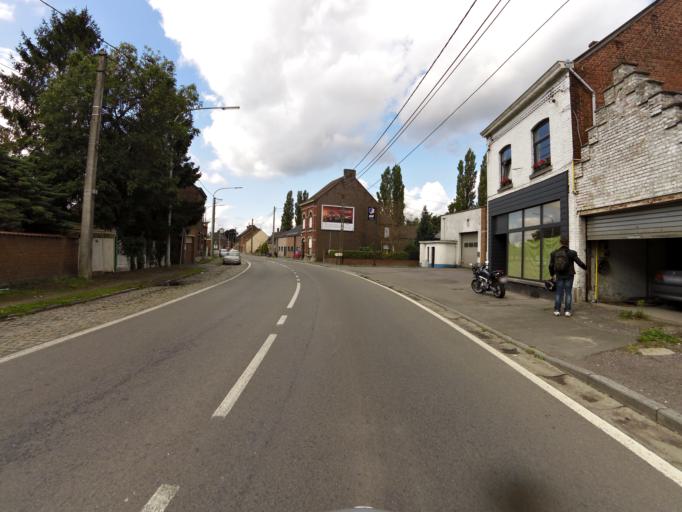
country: BE
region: Wallonia
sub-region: Province du Hainaut
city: Mons
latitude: 50.4732
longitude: 3.9069
